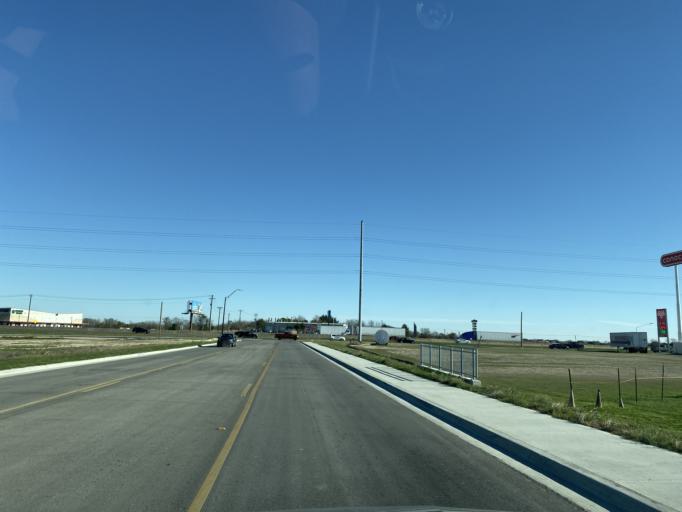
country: US
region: Texas
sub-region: Hays County
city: Kyle
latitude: 29.9997
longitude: -97.8703
